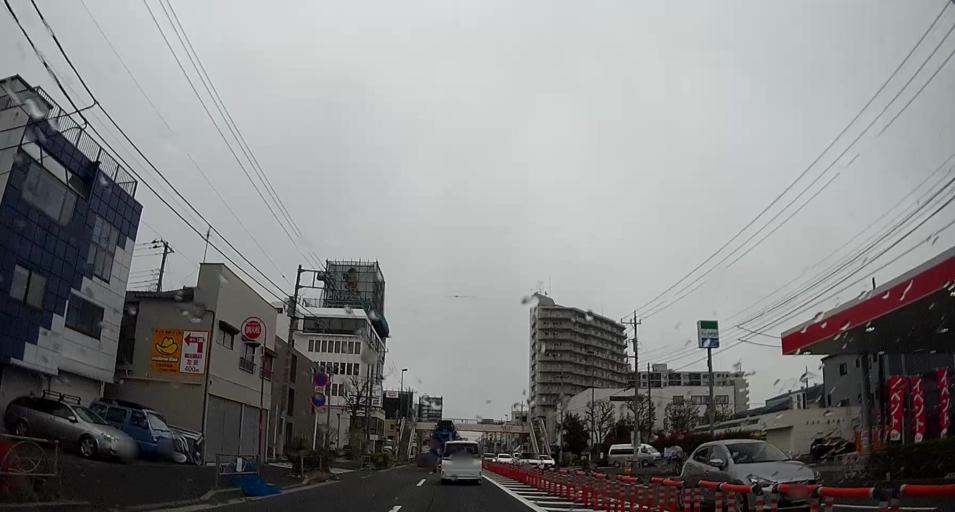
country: JP
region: Tokyo
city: Urayasu
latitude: 35.7032
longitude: 139.8700
